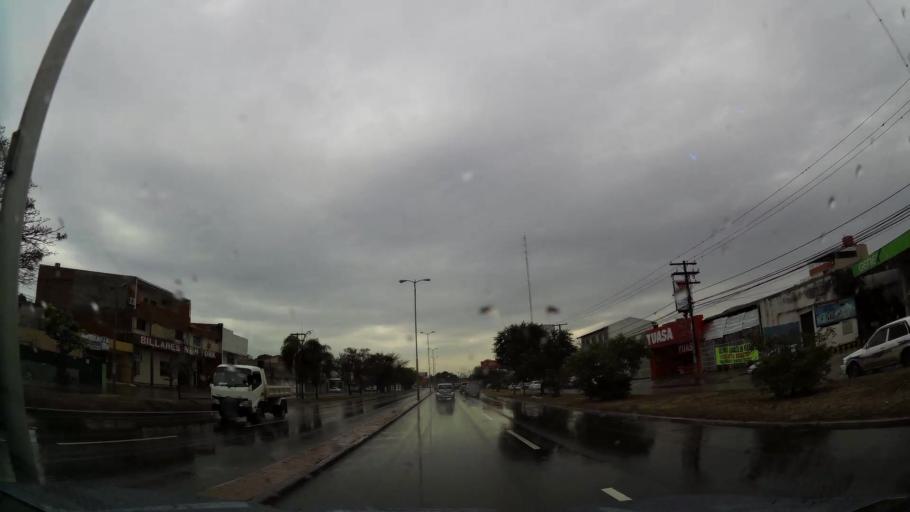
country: BO
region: Santa Cruz
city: Santa Cruz de la Sierra
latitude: -17.7901
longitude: -63.1652
